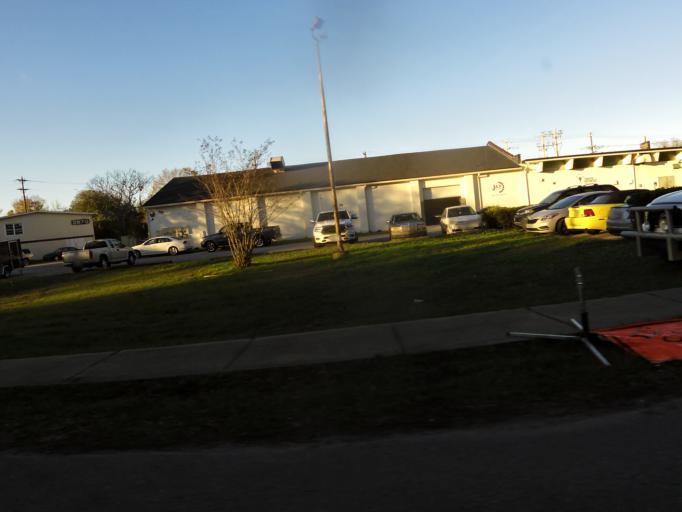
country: US
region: Florida
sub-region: Duval County
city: Jacksonville
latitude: 30.3184
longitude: -81.6949
